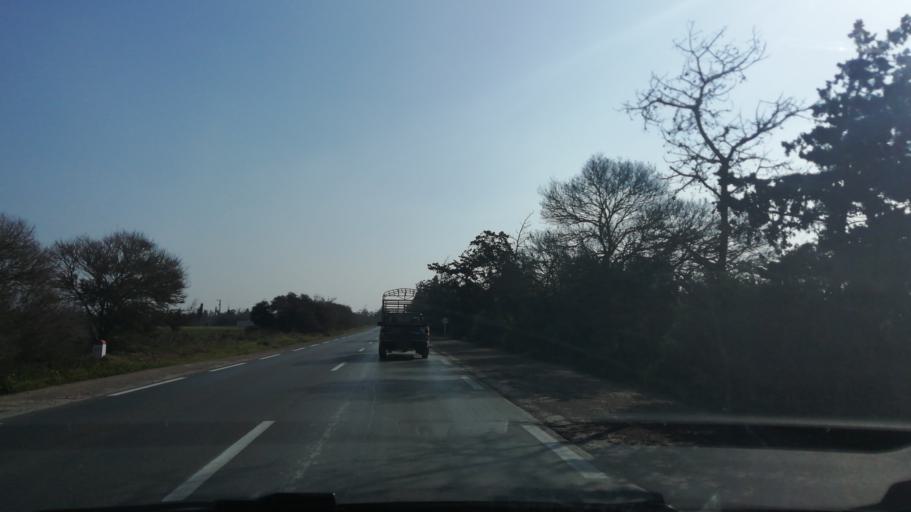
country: DZ
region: Mostaganem
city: Mostaganem
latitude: 35.7433
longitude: -0.0172
